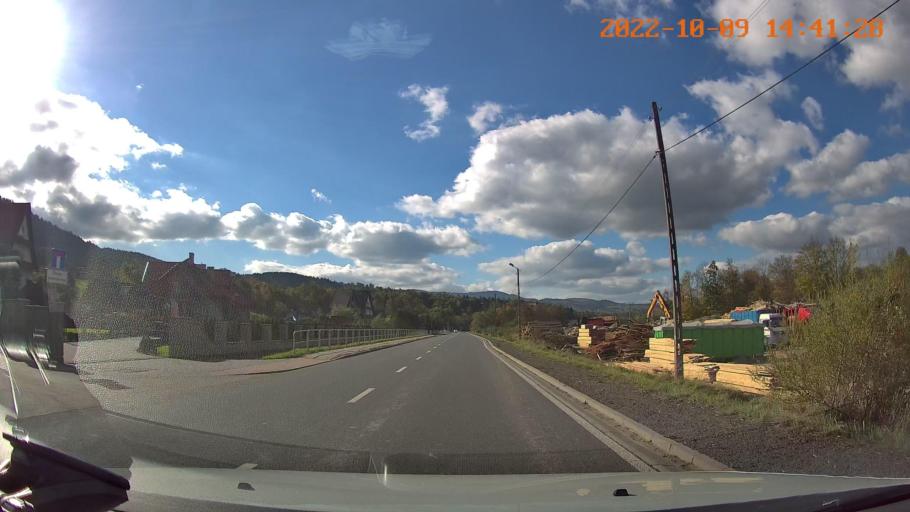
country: PL
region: Lesser Poland Voivodeship
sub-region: Powiat myslenicki
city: Lubien
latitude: 49.7100
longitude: 20.0134
